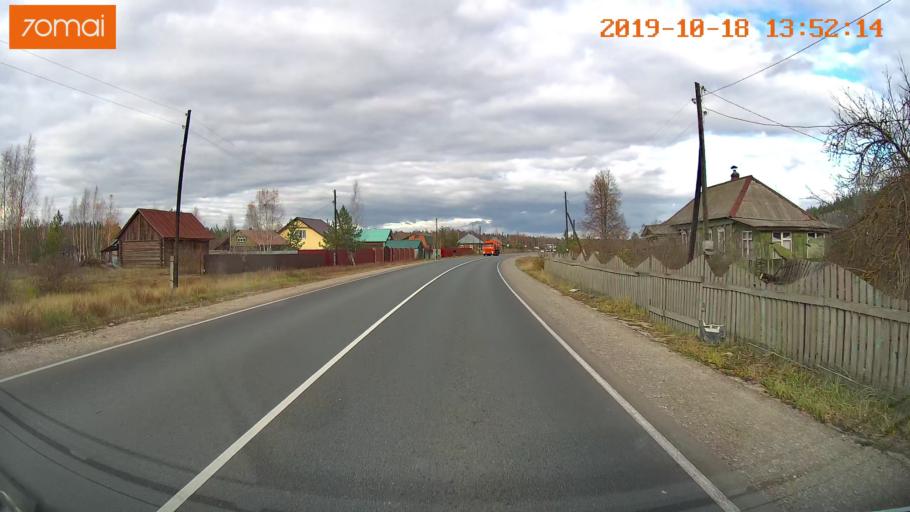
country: RU
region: Moskovskaya
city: Radovitskiy
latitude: 55.0277
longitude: 39.9665
